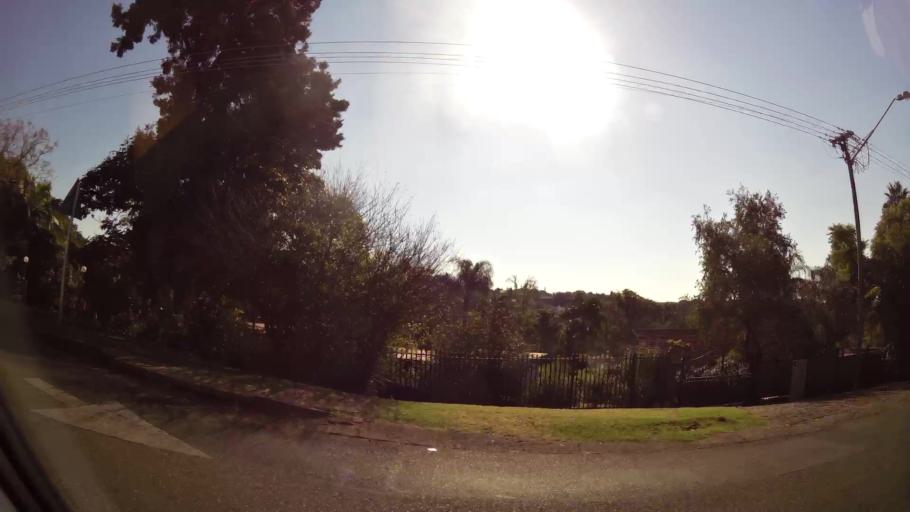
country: ZA
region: Gauteng
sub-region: City of Tshwane Metropolitan Municipality
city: Pretoria
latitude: -25.7895
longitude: 28.2474
